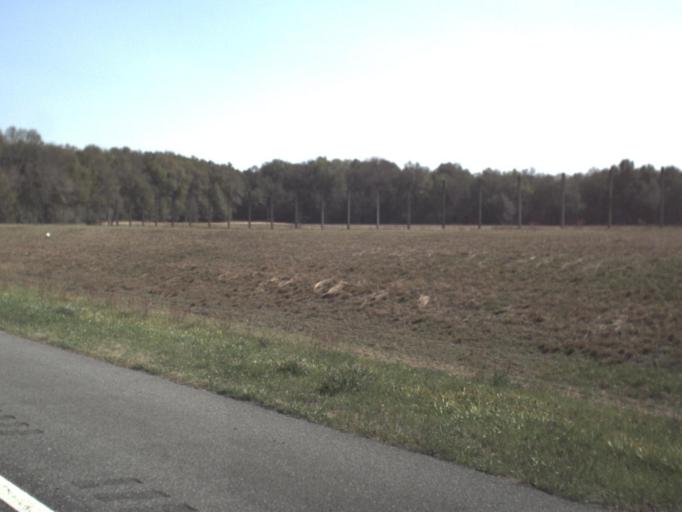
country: US
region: Florida
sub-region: Jackson County
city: Marianna
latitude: 30.6980
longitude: -85.1312
